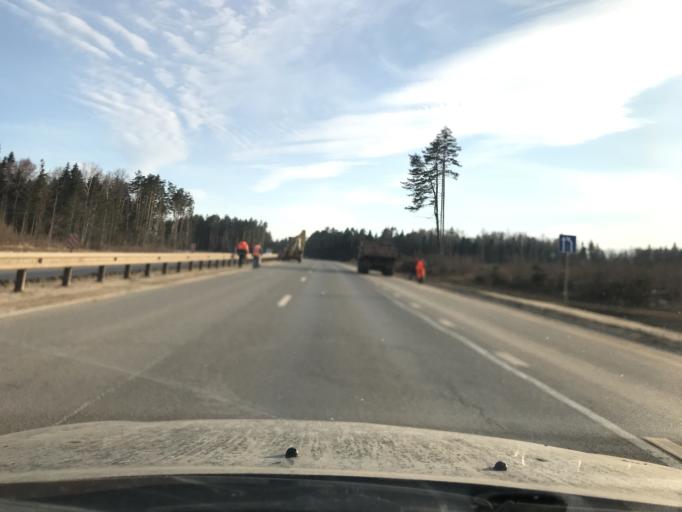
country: RU
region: Kaluga
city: Kaluga
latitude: 54.4188
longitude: 36.2020
